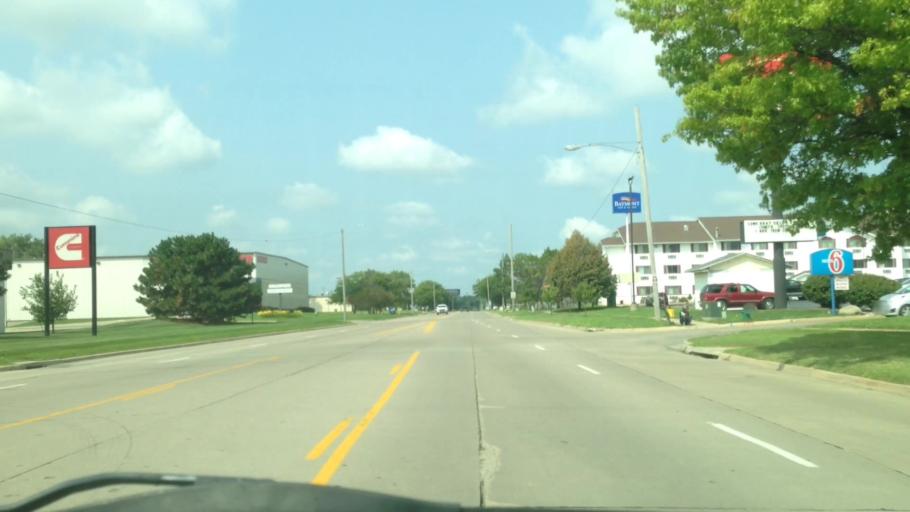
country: US
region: Iowa
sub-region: Linn County
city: Cedar Rapids
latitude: 41.9430
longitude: -91.6772
